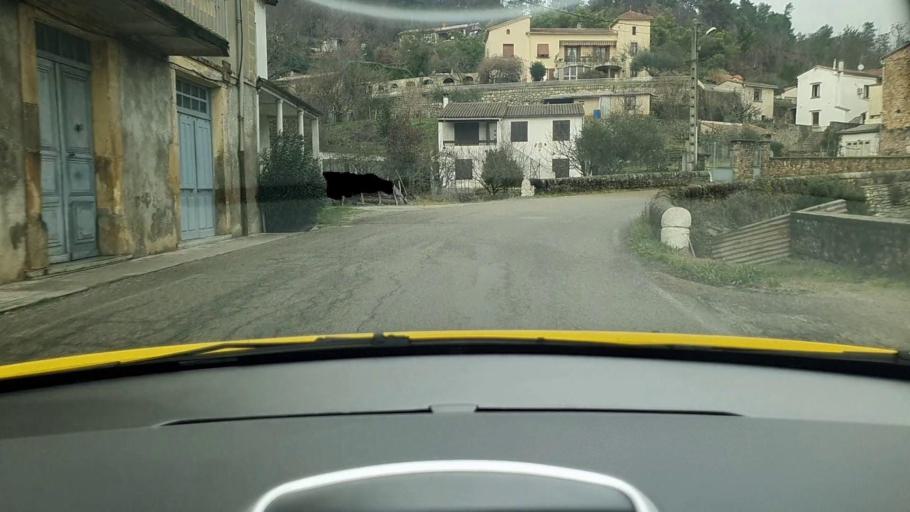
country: FR
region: Languedoc-Roussillon
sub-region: Departement du Gard
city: Besseges
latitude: 44.3019
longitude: 4.0928
